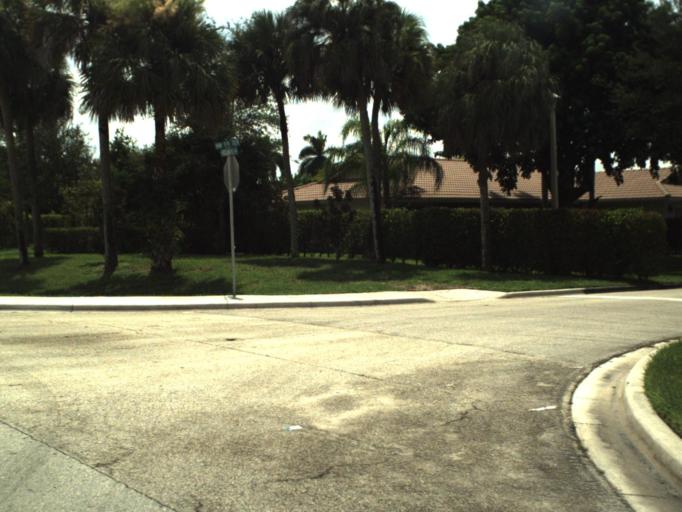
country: US
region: Florida
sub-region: Broward County
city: Tamarac
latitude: 26.2405
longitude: -80.2584
